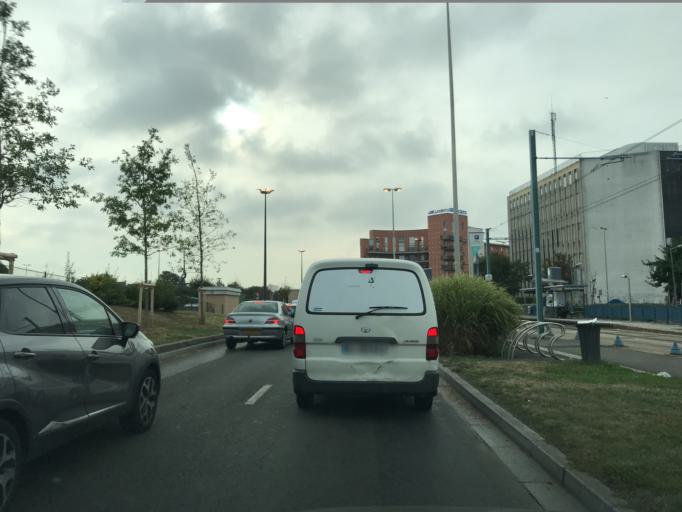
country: FR
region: Ile-de-France
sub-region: Departement de Seine-Saint-Denis
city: Drancy
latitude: 48.9130
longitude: 2.4350
